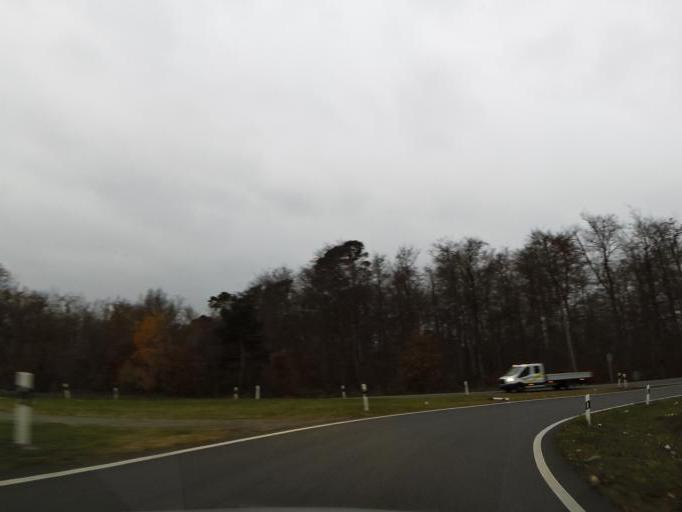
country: DE
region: Hesse
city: Kelsterbach
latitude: 50.0497
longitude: 8.5505
